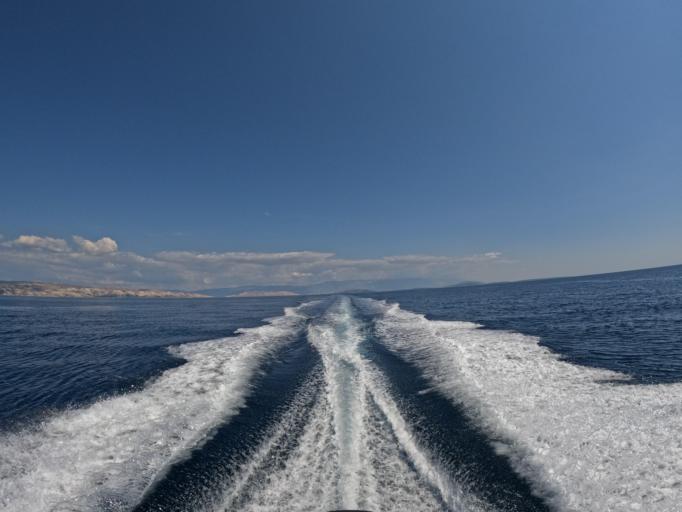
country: HR
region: Primorsko-Goranska
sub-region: Grad Krk
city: Krk
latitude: 44.9233
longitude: 14.5516
